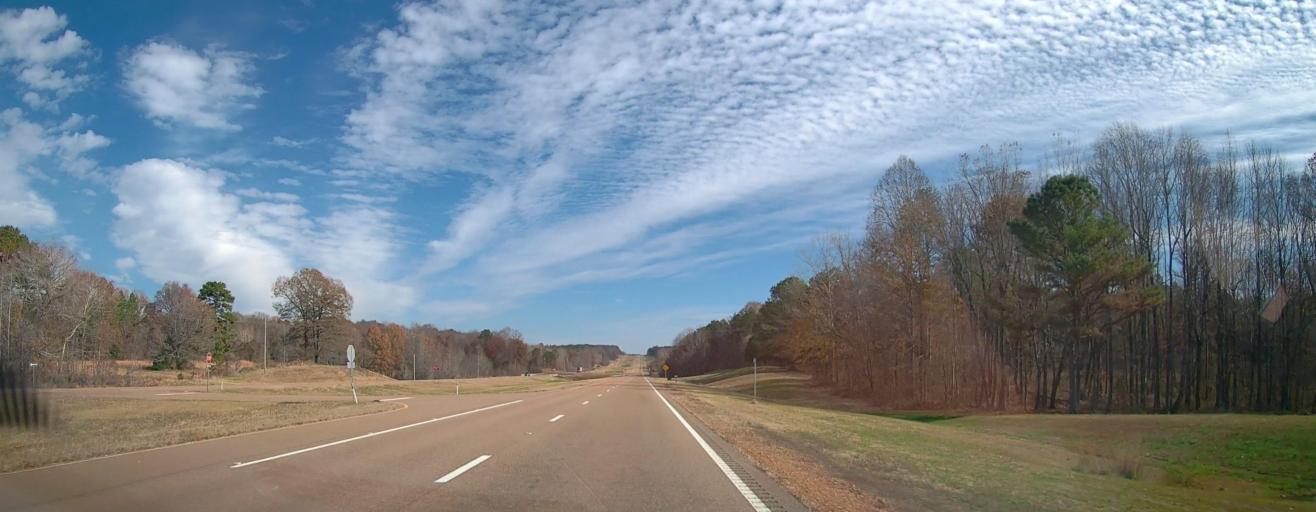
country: US
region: Mississippi
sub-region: Benton County
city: Ashland
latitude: 34.9515
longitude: -89.0659
